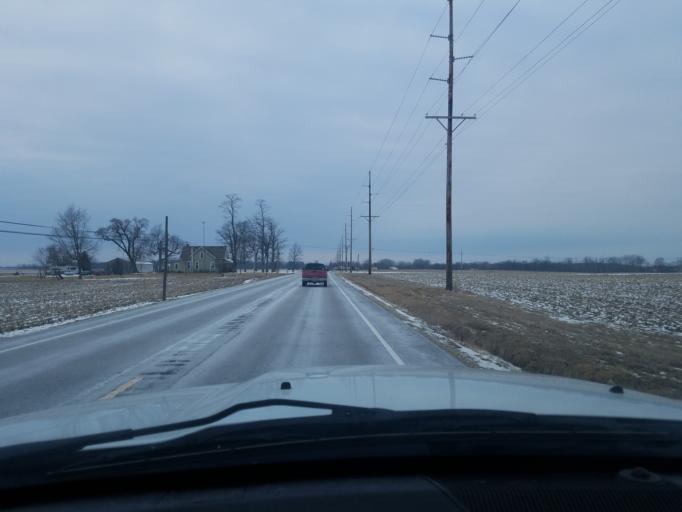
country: US
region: Indiana
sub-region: Randolph County
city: Winchester
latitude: 40.1714
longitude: -85.0475
